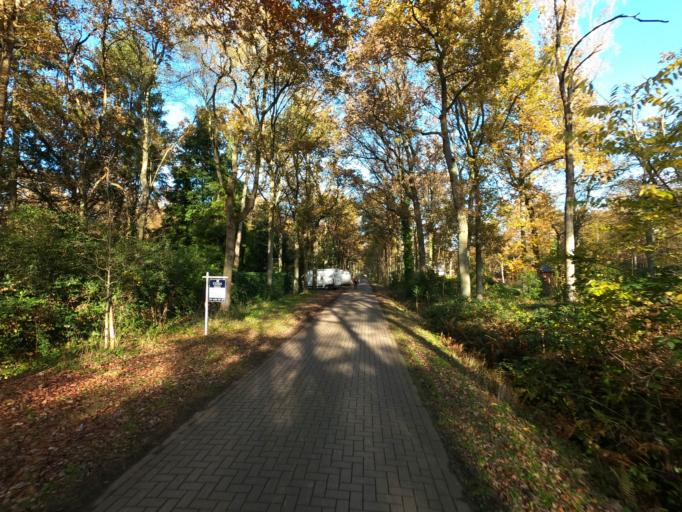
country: BE
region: Flanders
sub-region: Provincie Antwerpen
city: Brasschaat
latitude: 51.3438
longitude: 4.5277
